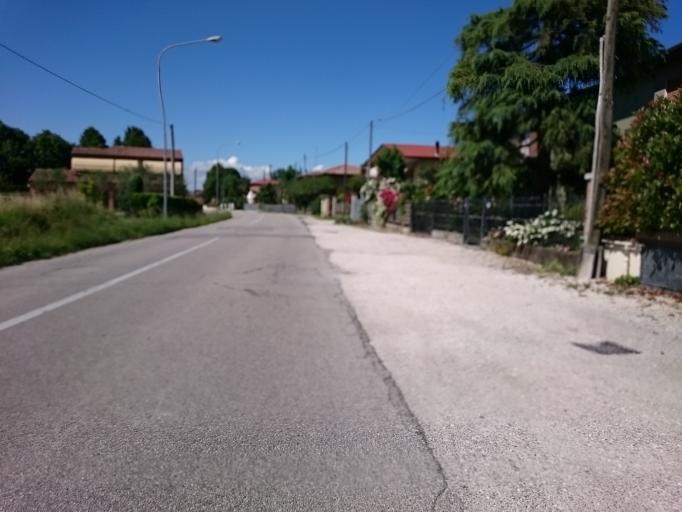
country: IT
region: Veneto
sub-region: Provincia di Padova
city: Piove di Sacco-Piovega
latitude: 45.2877
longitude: 12.0412
